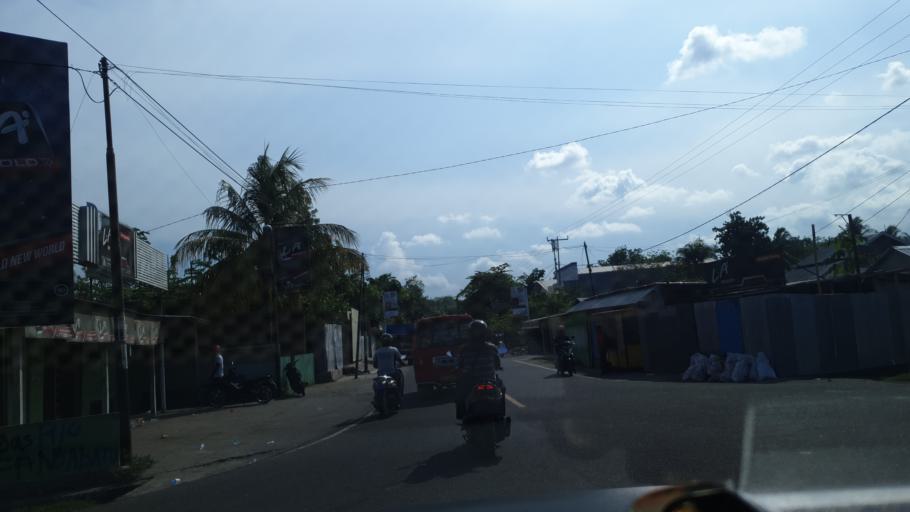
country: ID
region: East Nusa Tenggara
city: Nangalimang
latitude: -8.6381
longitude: 122.2087
